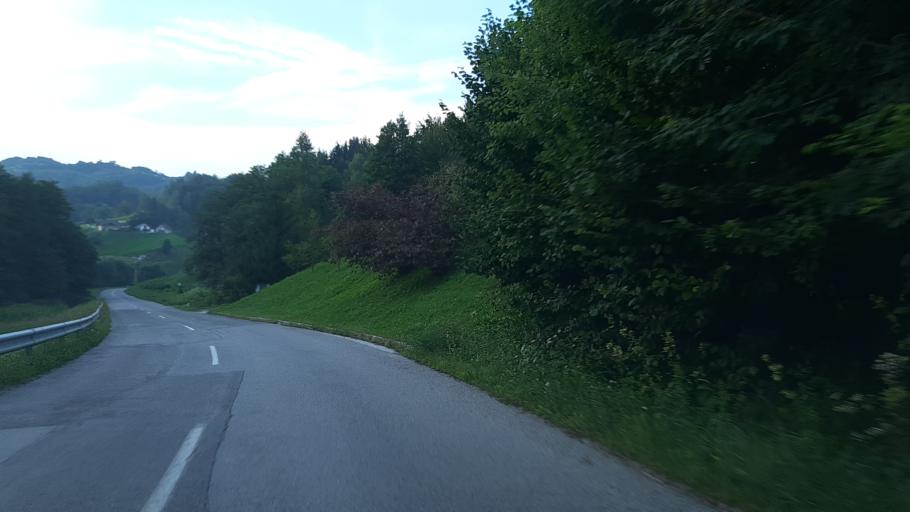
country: SI
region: Dobje
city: Dobje pri Planini
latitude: 46.1562
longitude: 15.4408
